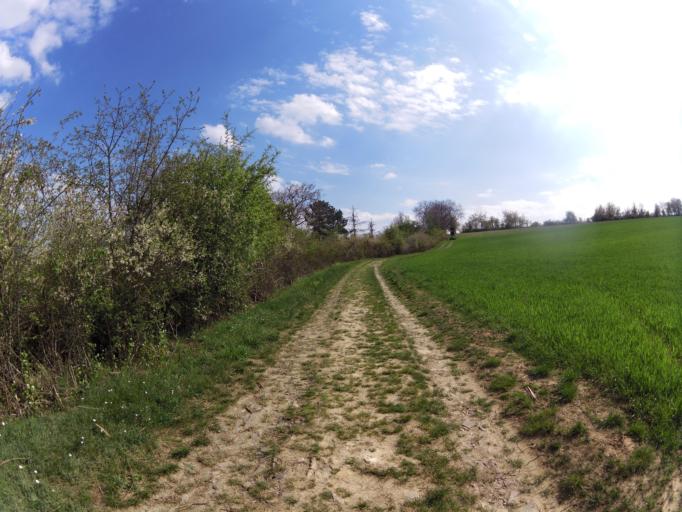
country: DE
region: Bavaria
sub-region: Regierungsbezirk Unterfranken
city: Sommerhausen
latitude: 49.6916
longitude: 10.0172
